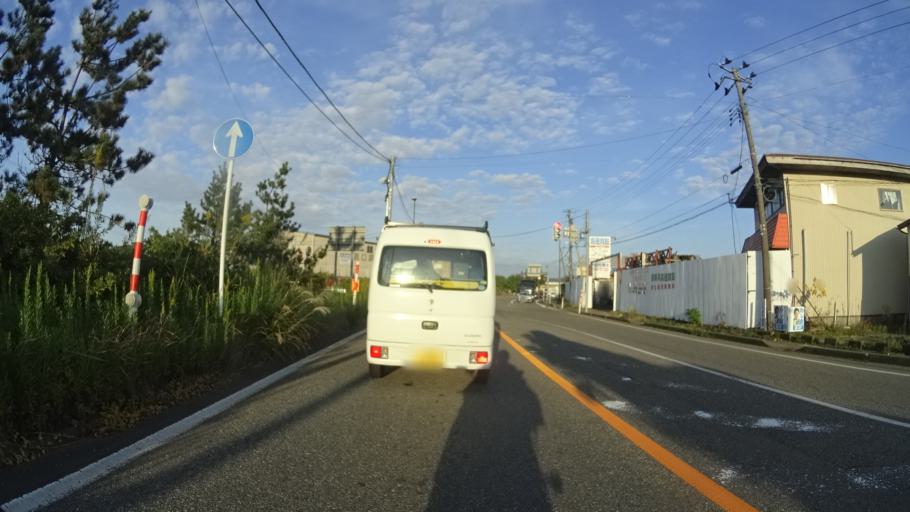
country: JP
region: Niigata
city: Kashiwazaki
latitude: 37.3976
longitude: 138.6045
